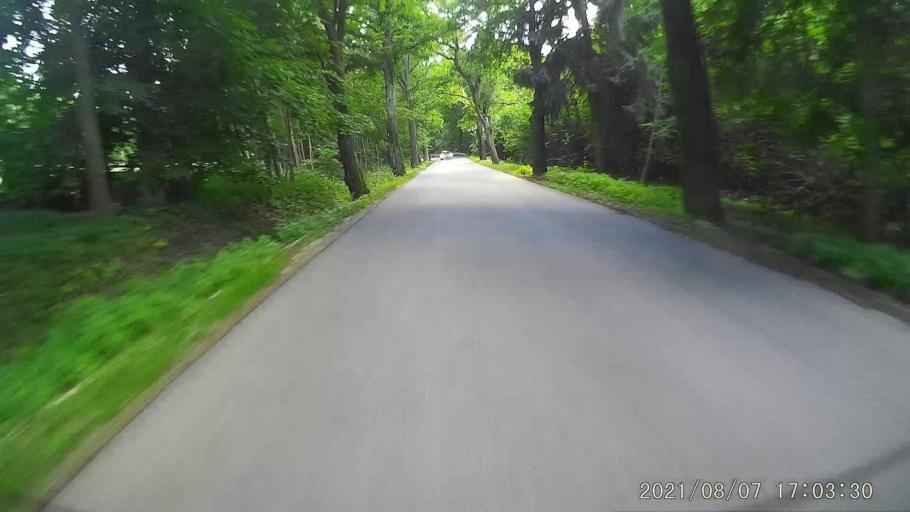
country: PL
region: Lower Silesian Voivodeship
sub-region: Powiat klodzki
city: Bystrzyca Klodzka
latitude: 50.2899
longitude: 16.5619
